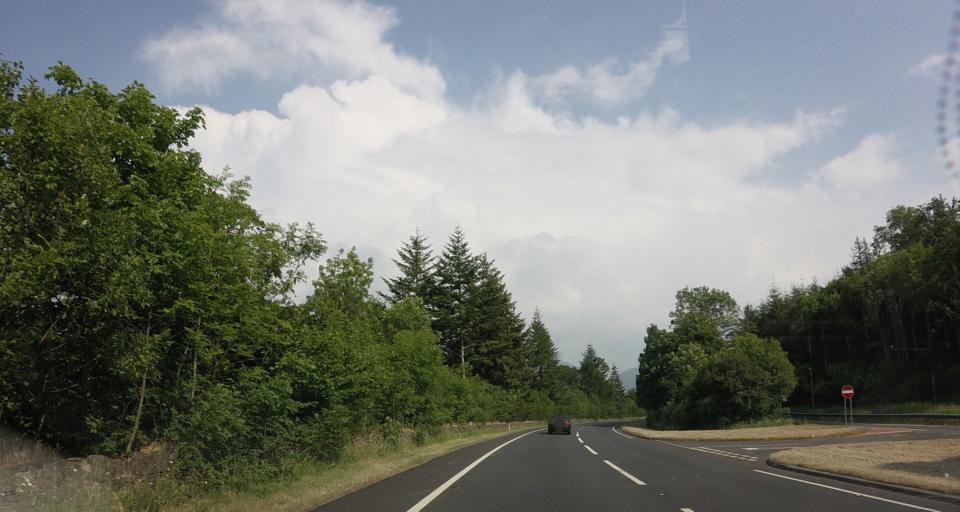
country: GB
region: England
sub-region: Cumbria
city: Keswick
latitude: 54.6656
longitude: -3.2331
